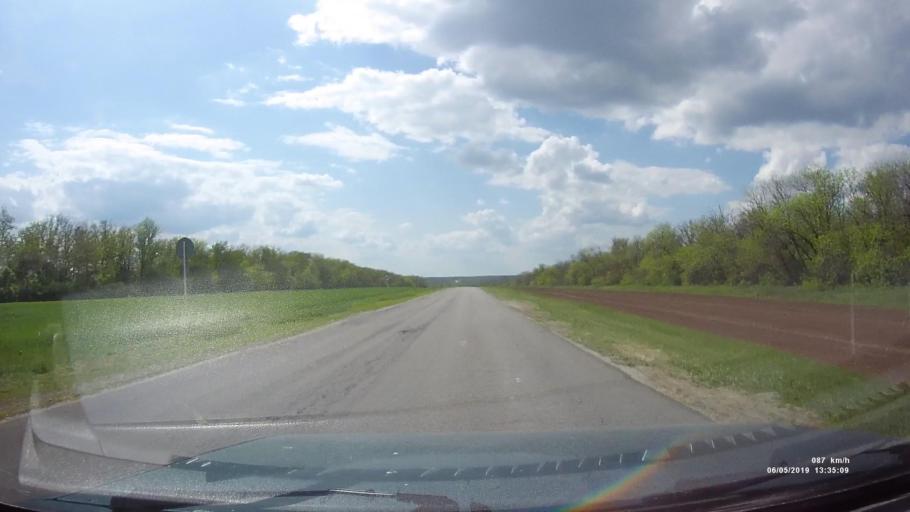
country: RU
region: Rostov
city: Ust'-Donetskiy
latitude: 47.6932
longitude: 40.7497
